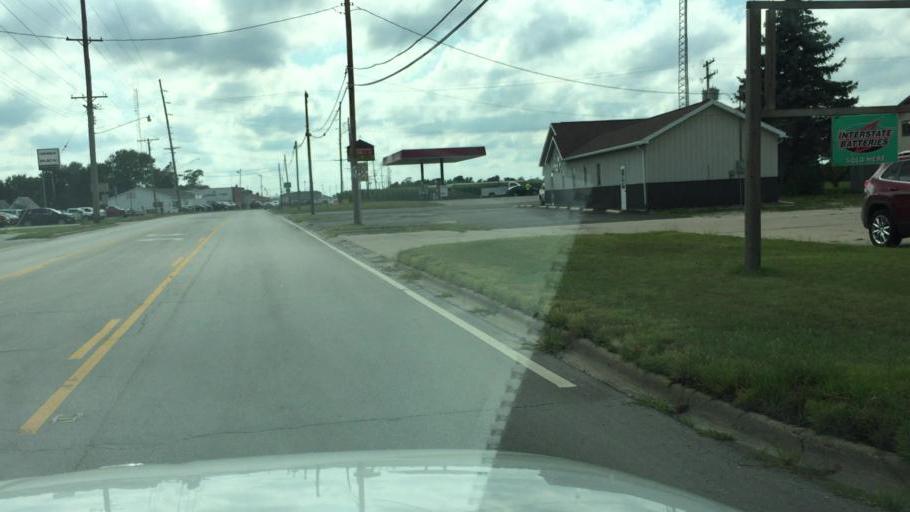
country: US
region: Illinois
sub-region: Hancock County
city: Carthage
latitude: 40.4163
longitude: -91.1411
